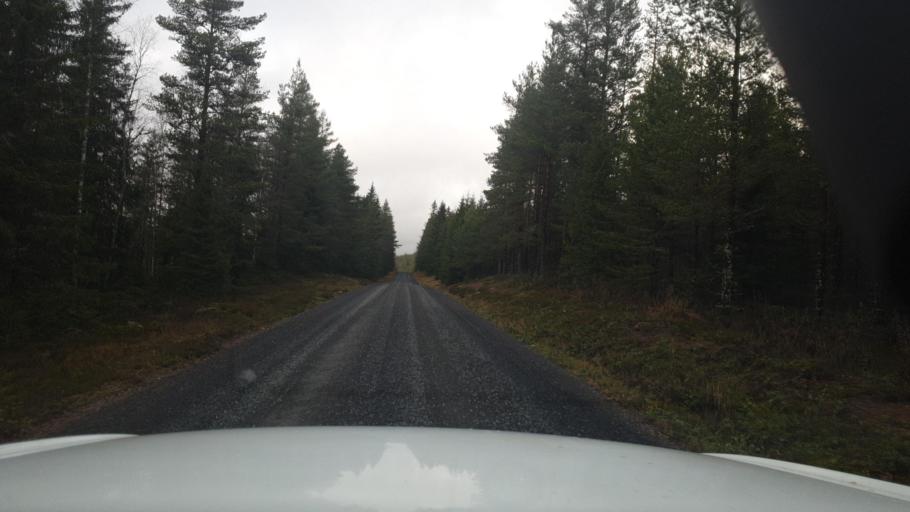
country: SE
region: Vaermland
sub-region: Eda Kommun
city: Charlottenberg
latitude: 60.1182
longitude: 12.6017
